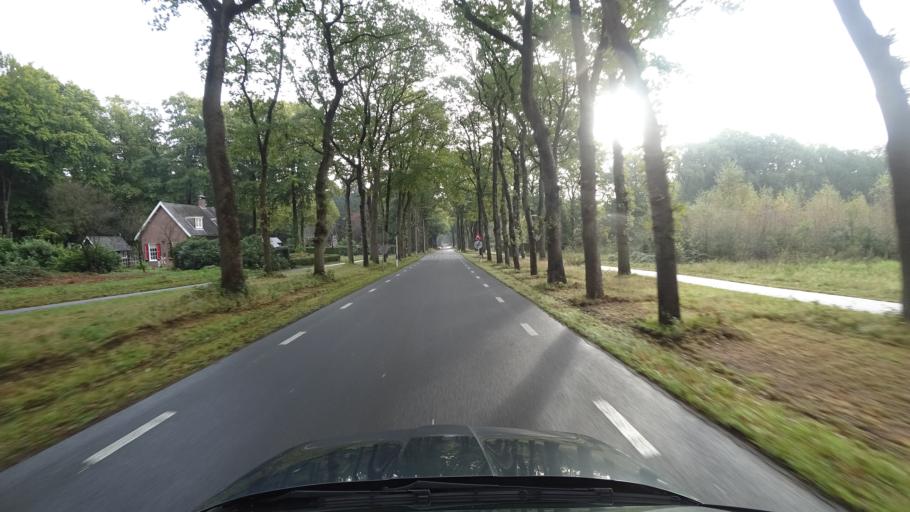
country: NL
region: Gelderland
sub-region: Gemeente Renkum
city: Renkum
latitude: 51.9917
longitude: 5.7139
